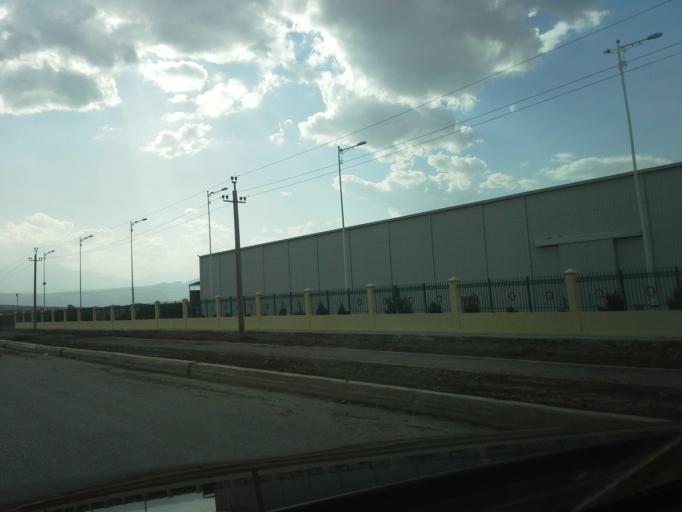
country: TM
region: Ahal
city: Ashgabat
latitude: 37.9912
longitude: 58.3010
